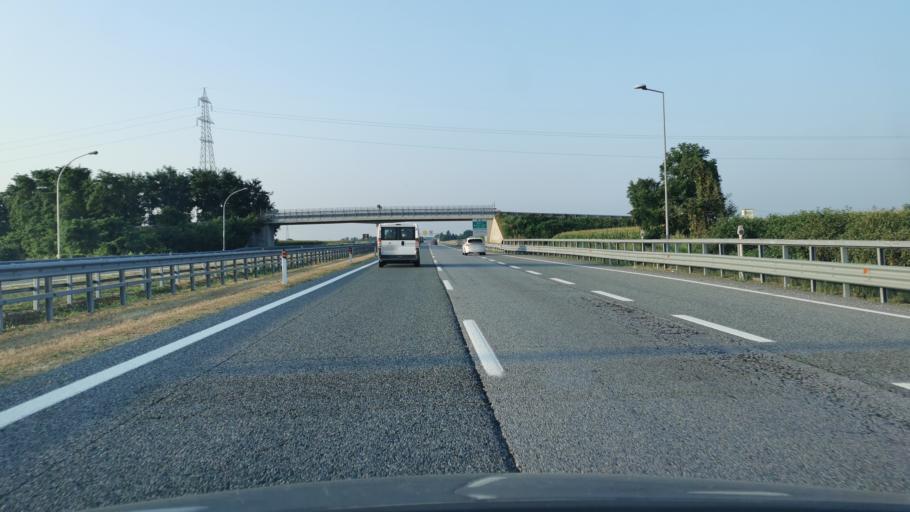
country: IT
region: Piedmont
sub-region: Provincia di Torino
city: Carmagnola
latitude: 44.8713
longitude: 7.7472
